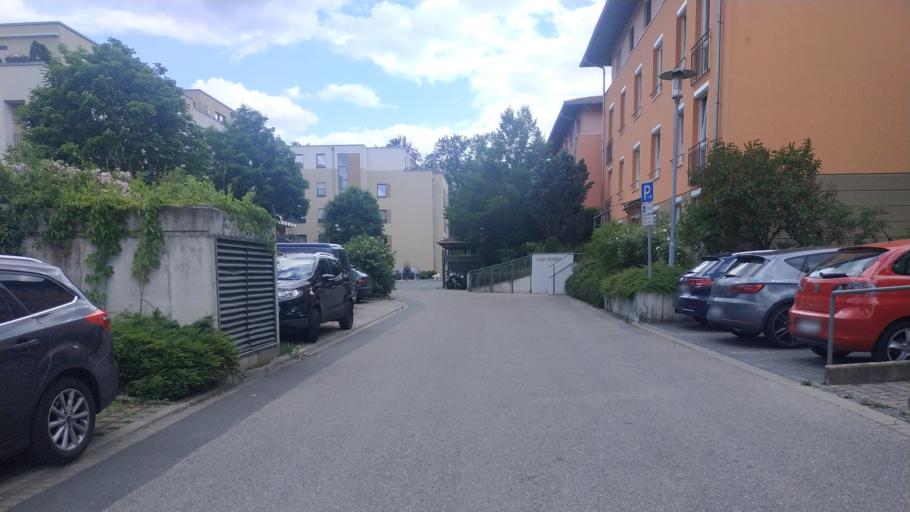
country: DE
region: Bavaria
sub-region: Regierungsbezirk Mittelfranken
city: Nuernberg
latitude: 49.4311
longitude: 11.0889
